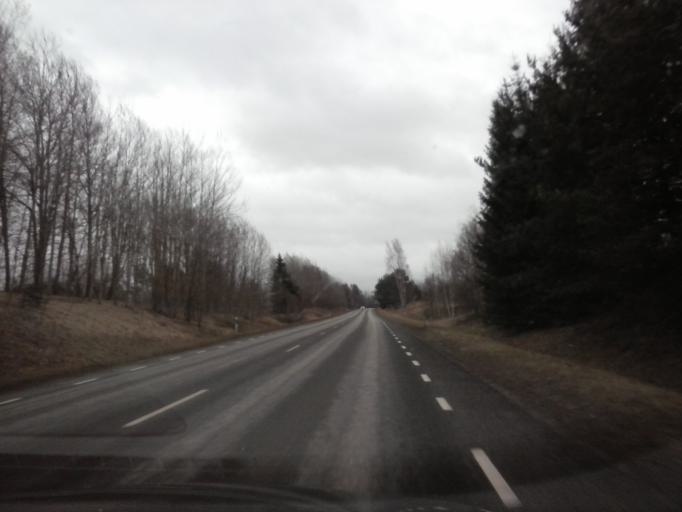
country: EE
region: Tartu
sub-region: UElenurme vald
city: Ulenurme
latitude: 58.2587
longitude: 26.7799
